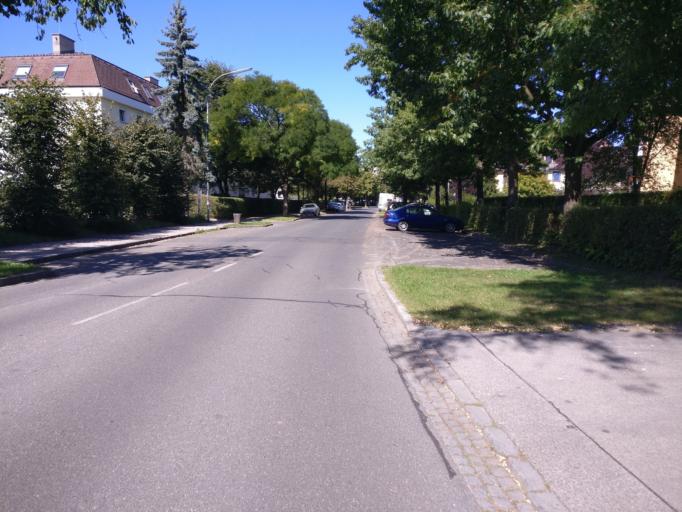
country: AT
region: Carinthia
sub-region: Klagenfurt am Woerthersee
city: Klagenfurt am Woerthersee
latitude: 46.6132
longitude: 14.2786
